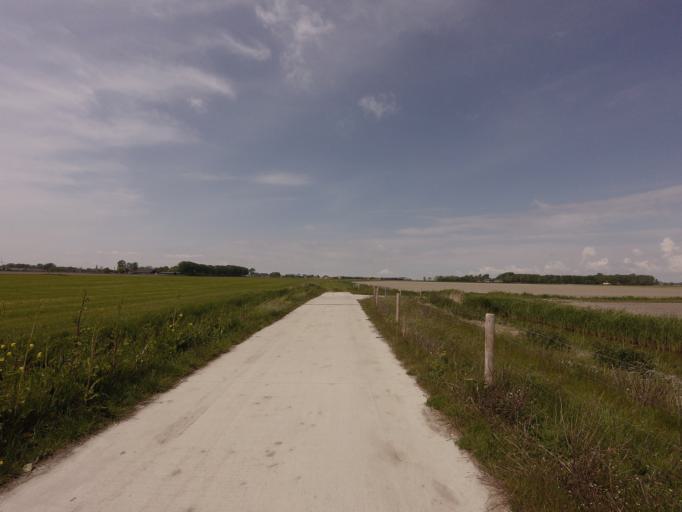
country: NL
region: Friesland
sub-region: Sudwest Fryslan
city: Bolsward
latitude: 53.1032
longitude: 5.4847
